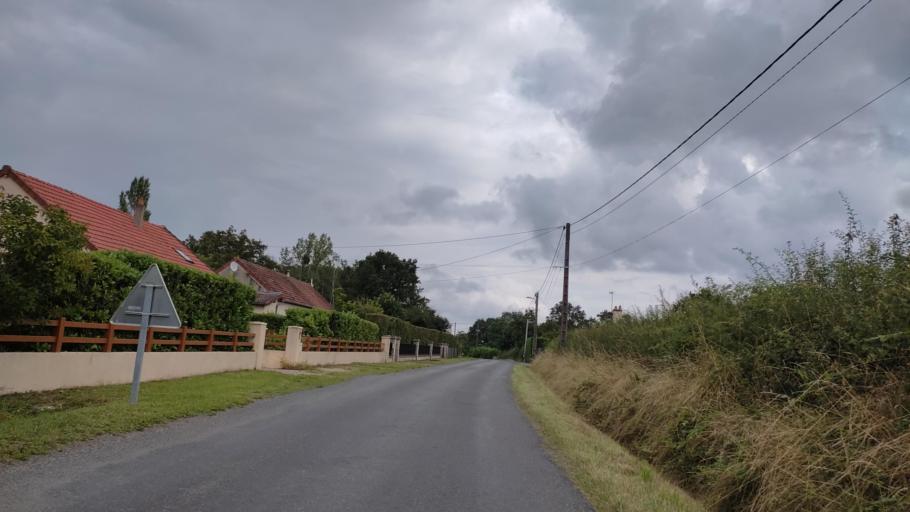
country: FR
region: Bourgogne
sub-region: Departement de la Nievre
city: Cercy-la-Tour
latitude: 46.7928
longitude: 3.6148
